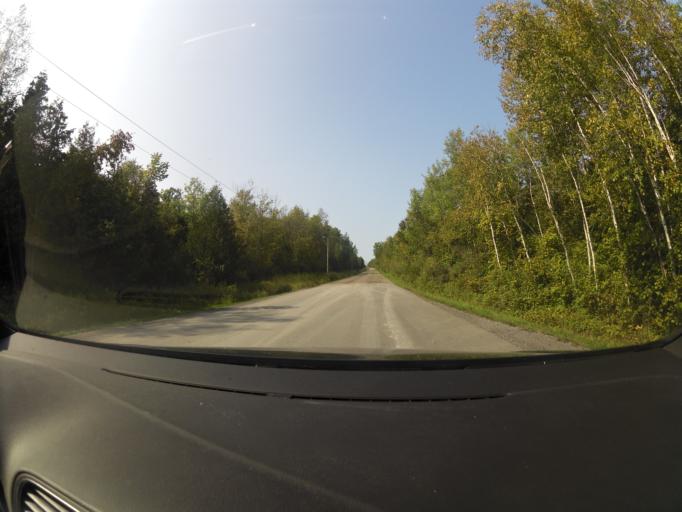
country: CA
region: Ontario
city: Carleton Place
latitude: 45.3063
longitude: -76.1276
